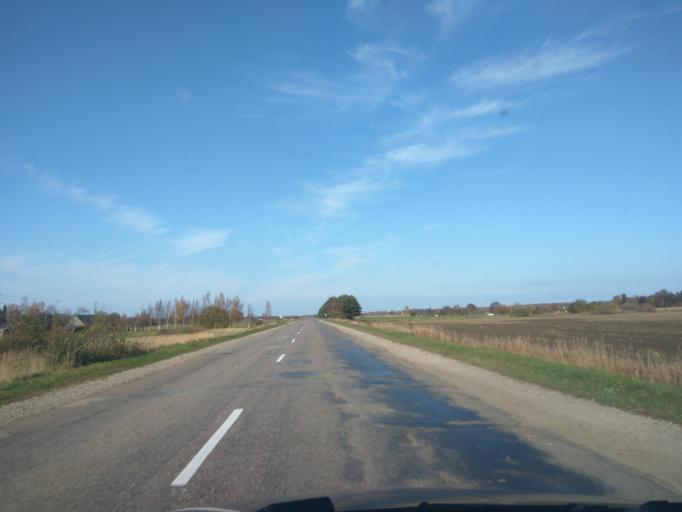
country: LV
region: Ventspils Rajons
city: Piltene
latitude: 57.2353
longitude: 21.5990
